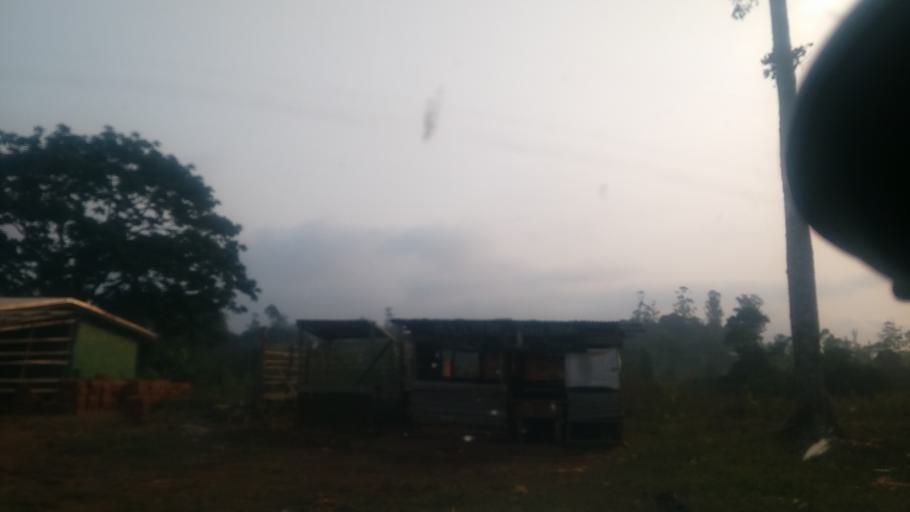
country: CM
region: West
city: Bana
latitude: 5.1400
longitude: 10.2792
